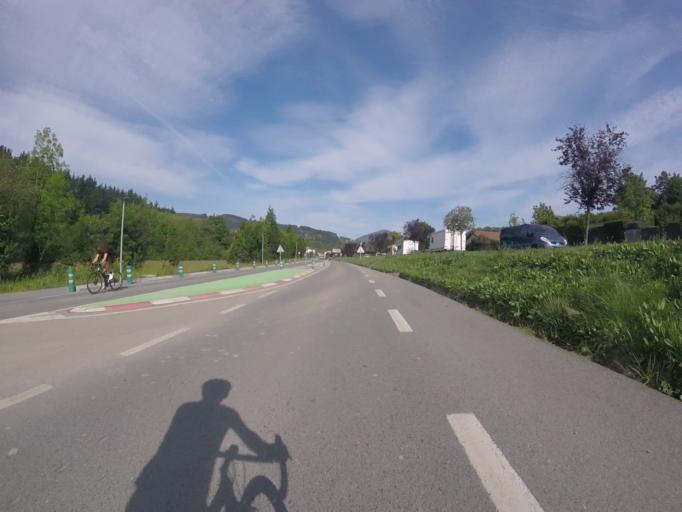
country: ES
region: Basque Country
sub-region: Provincia de Guipuzcoa
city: Gabiria
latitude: 43.0665
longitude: -2.2786
